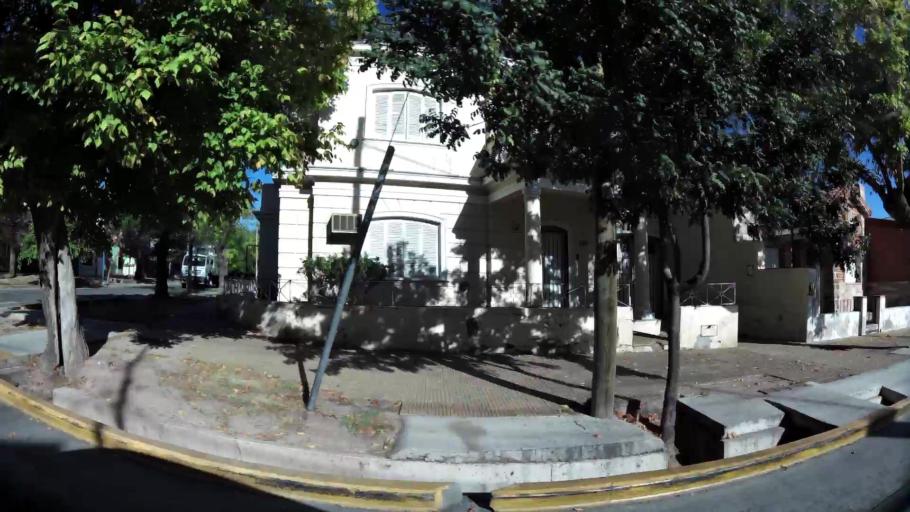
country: AR
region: Mendoza
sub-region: Departamento de Godoy Cruz
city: Godoy Cruz
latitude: -32.9343
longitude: -68.8479
